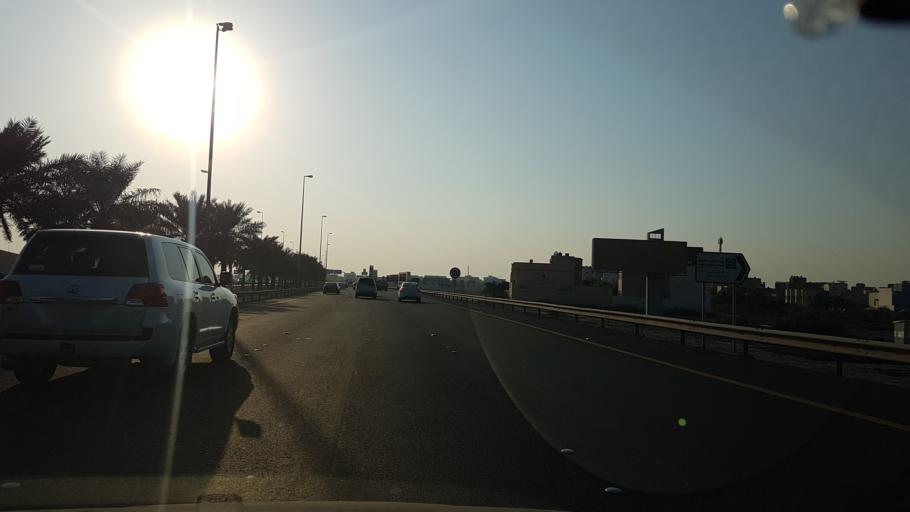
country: BH
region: Northern
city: Madinat `Isa
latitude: 26.1937
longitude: 50.5198
